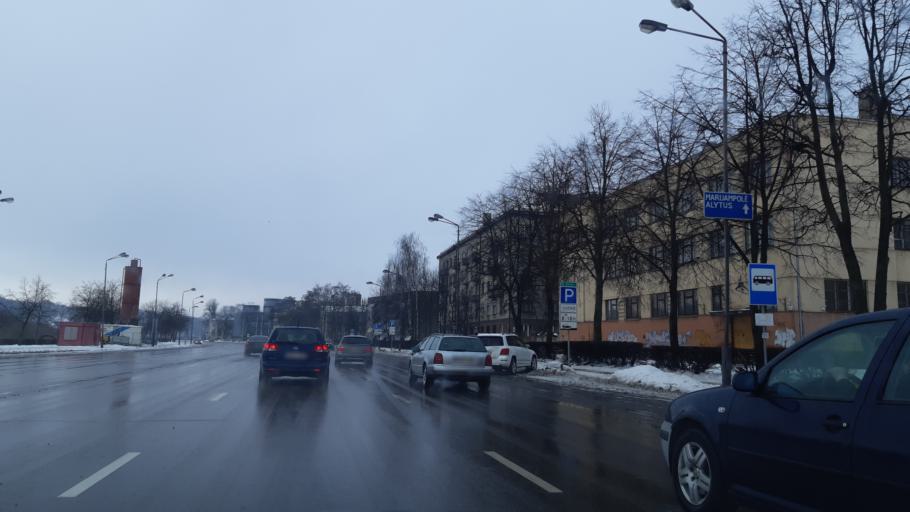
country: LT
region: Kauno apskritis
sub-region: Kaunas
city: Kaunas
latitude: 54.8947
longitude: 23.9074
